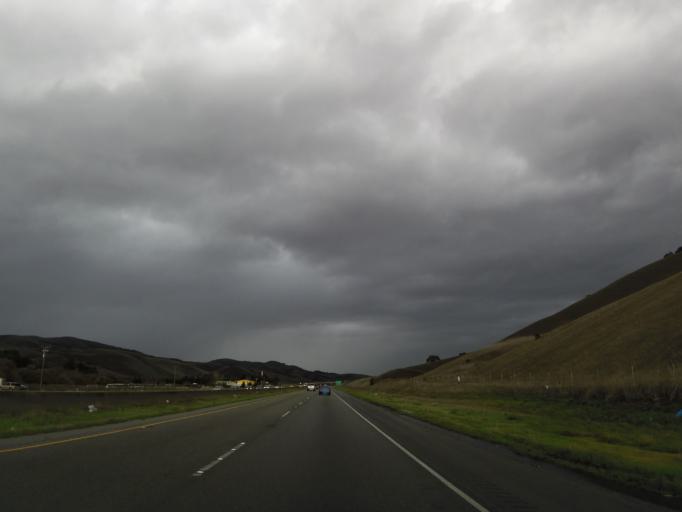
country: US
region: California
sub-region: San Benito County
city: San Juan Bautista
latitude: 36.8952
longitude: -121.5562
